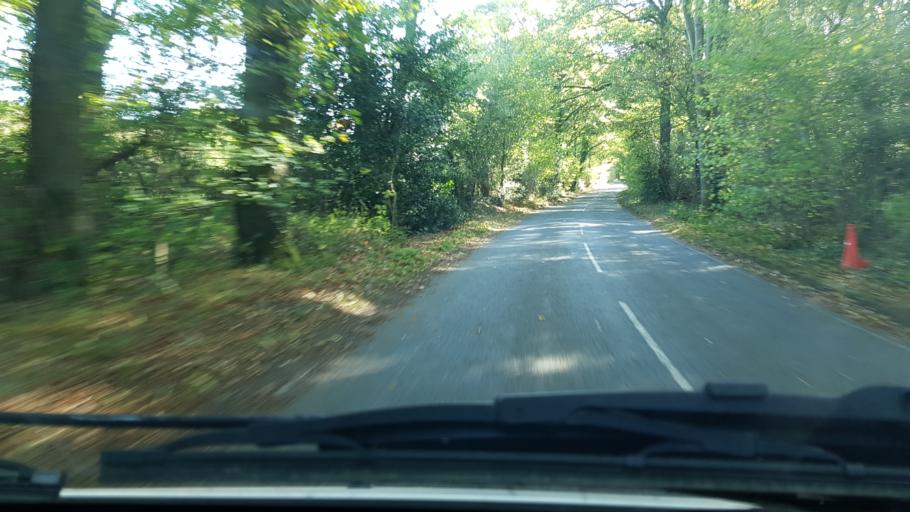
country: GB
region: England
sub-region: Surrey
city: Ockley
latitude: 51.1283
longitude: -0.3992
